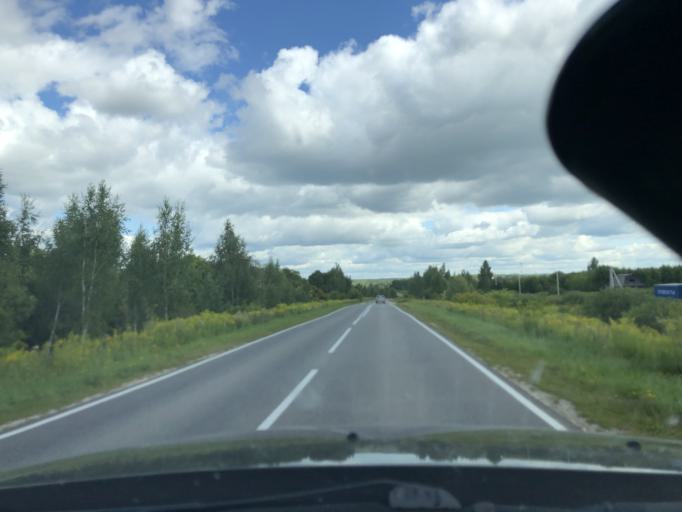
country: RU
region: Tula
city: Yasnogorsk
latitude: 54.4414
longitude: 37.7027
